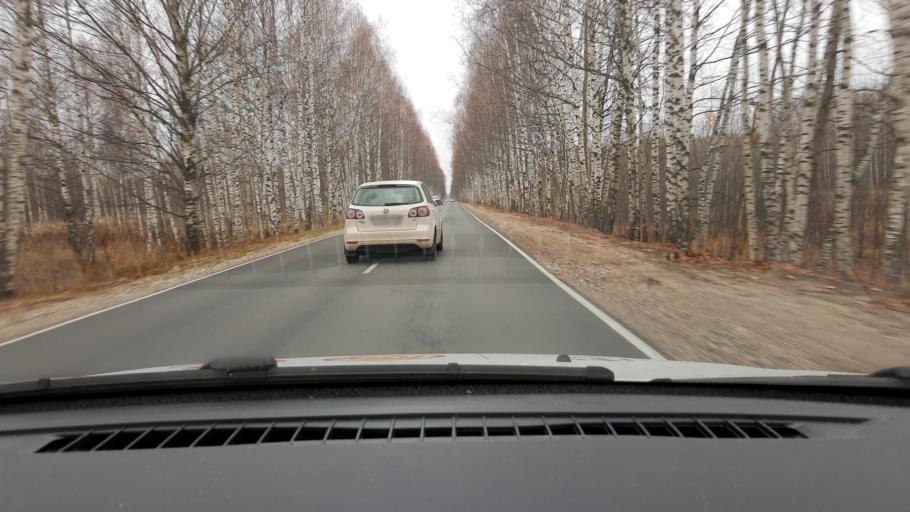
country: RU
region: Nizjnij Novgorod
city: Neklyudovo
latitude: 56.4852
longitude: 43.8662
